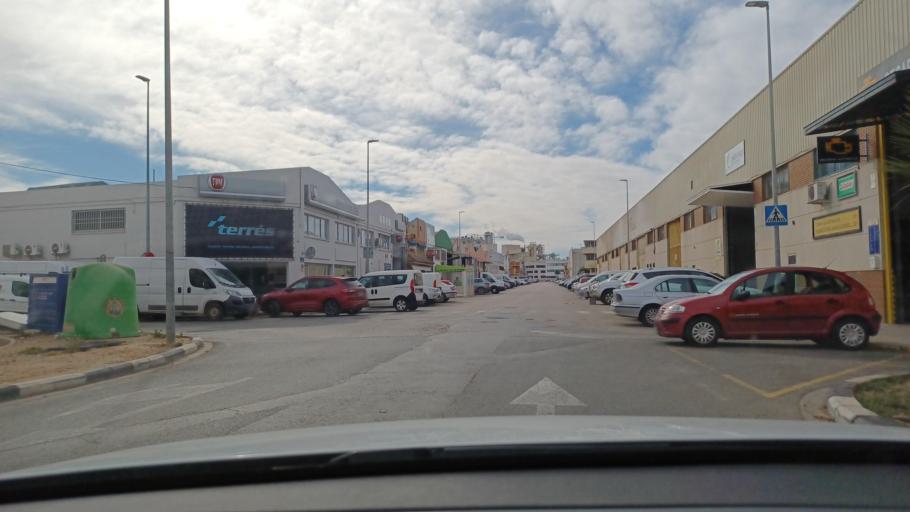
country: ES
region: Valencia
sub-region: Provincia de Valencia
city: Benifaio
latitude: 39.2878
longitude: -0.4323
